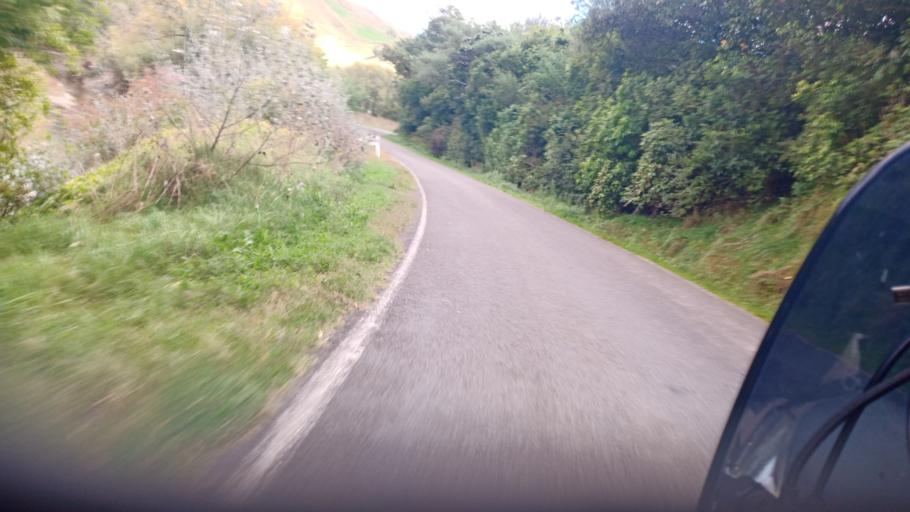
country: NZ
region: Gisborne
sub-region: Gisborne District
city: Gisborne
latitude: -38.4317
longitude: 177.7414
